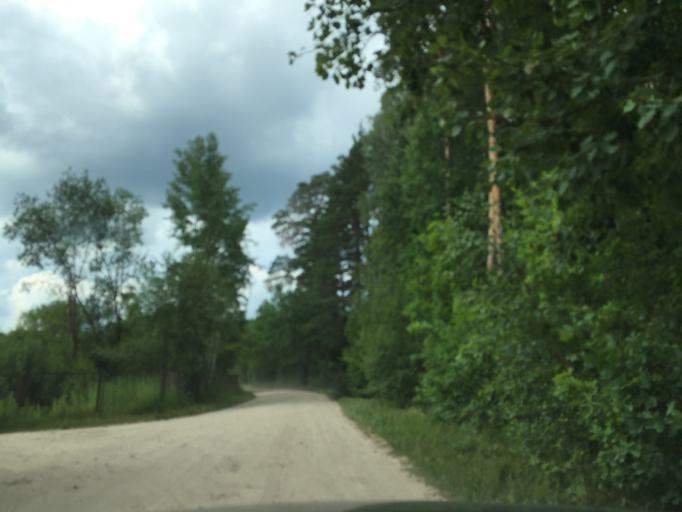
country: LV
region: Jelgava
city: Jelgava
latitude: 56.6259
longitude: 23.6259
